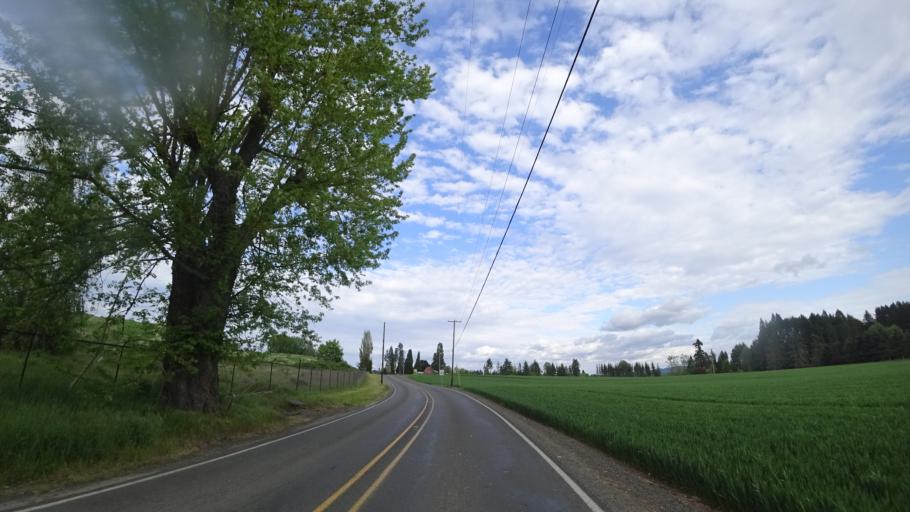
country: US
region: Oregon
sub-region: Washington County
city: Hillsboro
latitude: 45.4867
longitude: -122.9778
